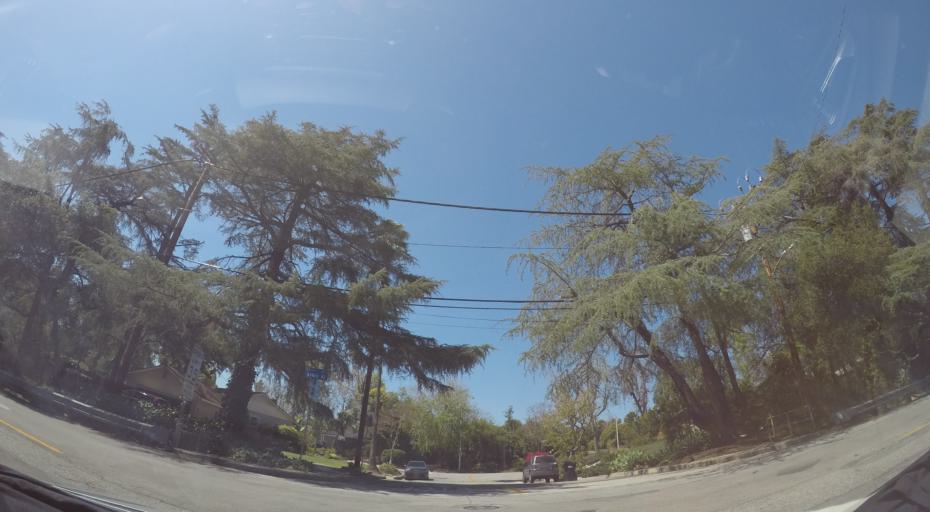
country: US
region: California
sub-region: Los Angeles County
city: Altadena
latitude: 34.1845
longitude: -118.1112
